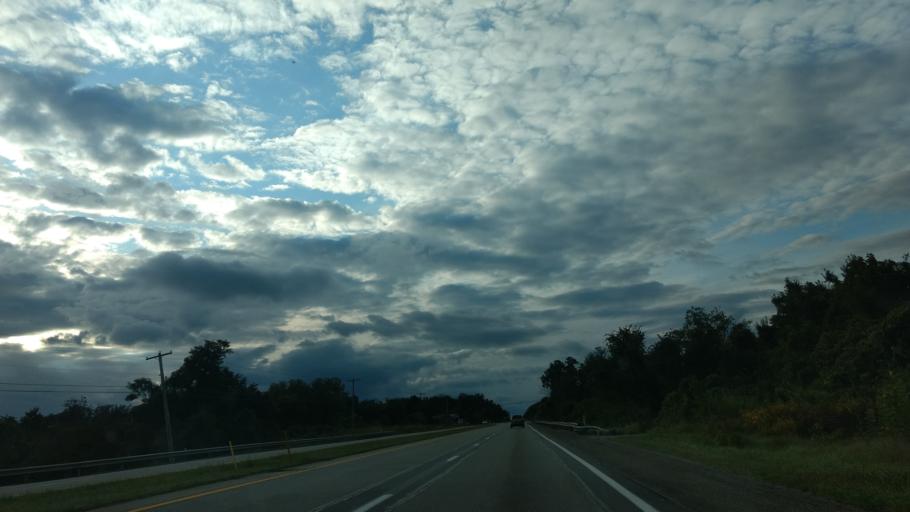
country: US
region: Pennsylvania
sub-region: Westmoreland County
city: Fellsburg
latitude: 40.1702
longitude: -79.7941
